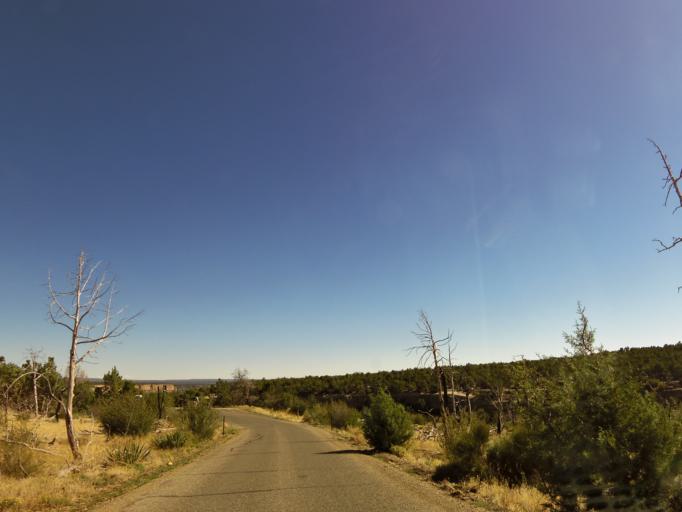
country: US
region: Colorado
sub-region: Montezuma County
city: Cortez
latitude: 37.1655
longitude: -108.4768
